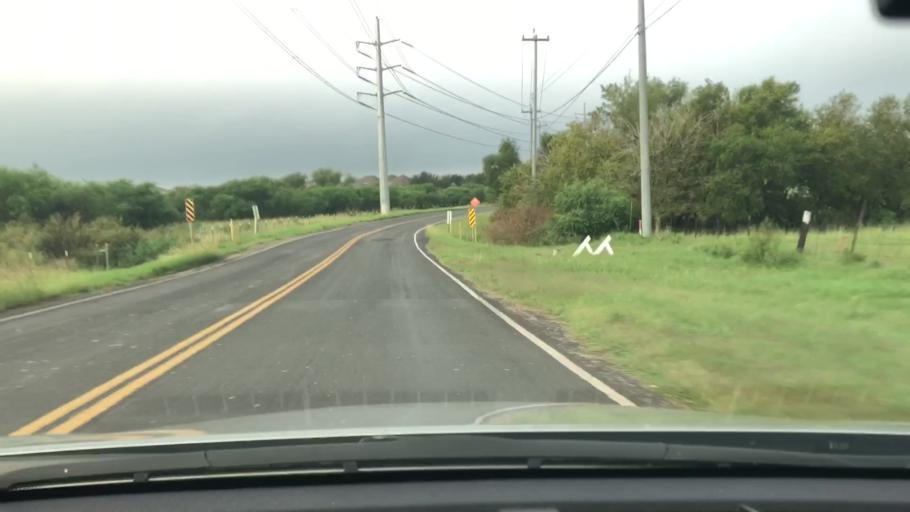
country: US
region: Texas
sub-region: Bexar County
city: Converse
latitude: 29.4678
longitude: -98.3280
